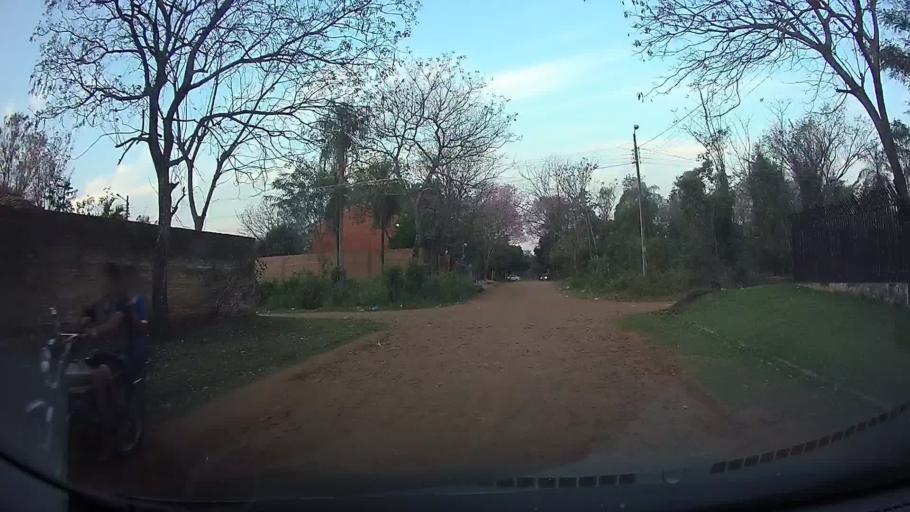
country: PY
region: Central
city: Limpio
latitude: -25.2296
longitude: -57.4697
